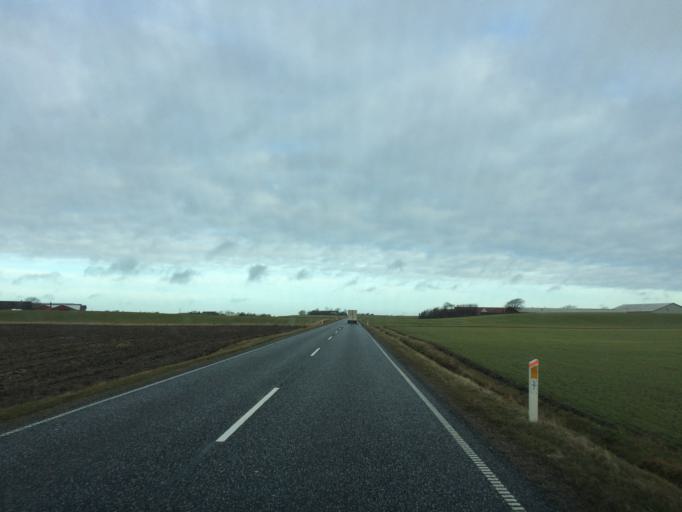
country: DK
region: Central Jutland
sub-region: Struer Kommune
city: Struer
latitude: 56.4524
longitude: 8.5386
